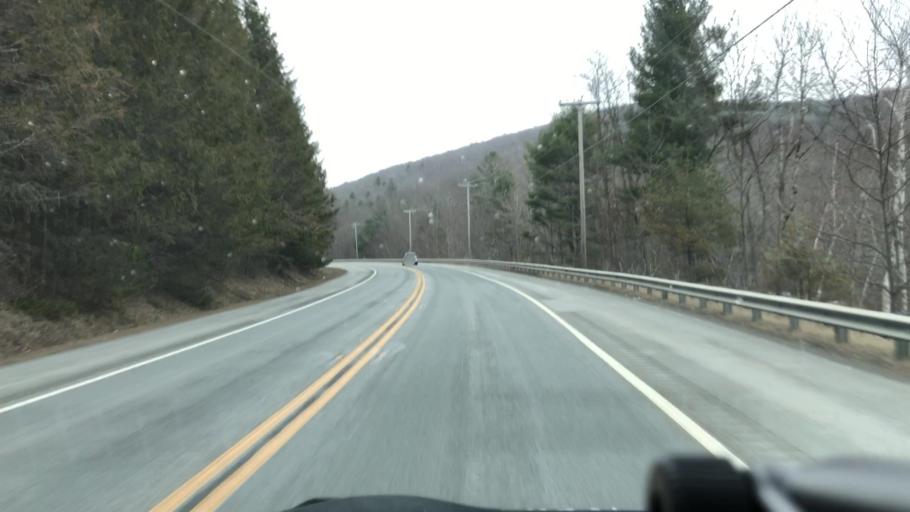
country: US
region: Massachusetts
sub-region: Hampshire County
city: Chesterfield
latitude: 42.4880
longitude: -72.9488
